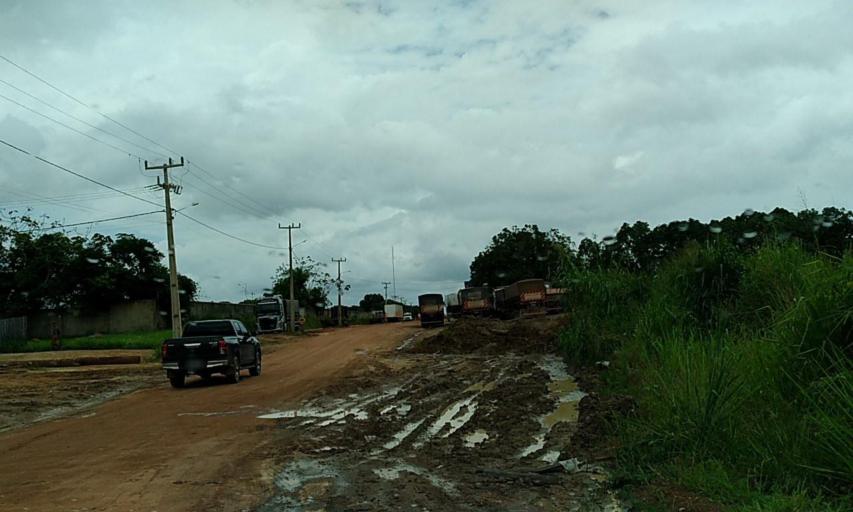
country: BR
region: Para
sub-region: Senador Jose Porfirio
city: Senador Jose Porfirio
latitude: -2.5846
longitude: -51.9434
